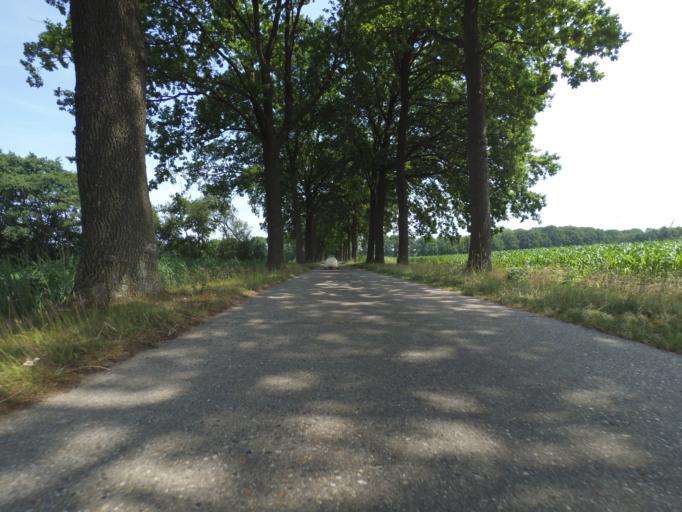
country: NL
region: North Brabant
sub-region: Gemeente Zundert
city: Zundert
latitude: 51.4323
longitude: 4.6932
